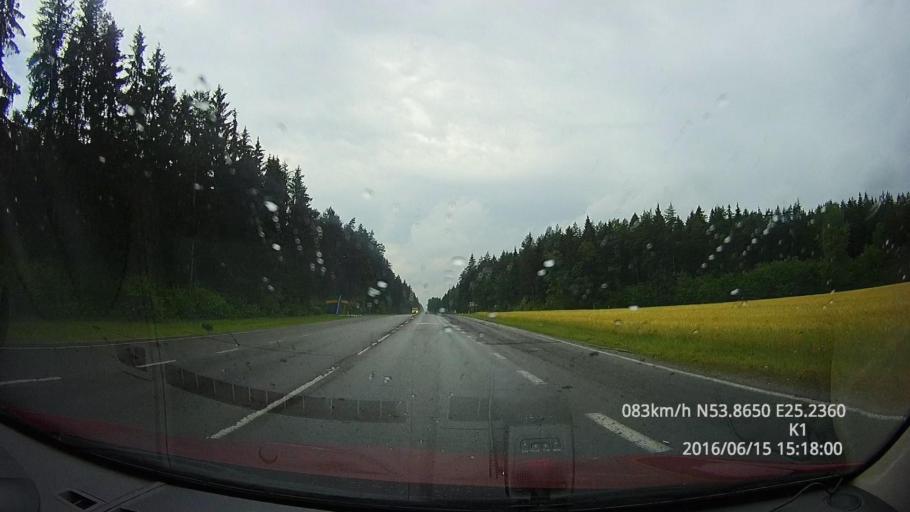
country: BY
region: Grodnenskaya
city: Lida
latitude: 53.8649
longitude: 25.2357
